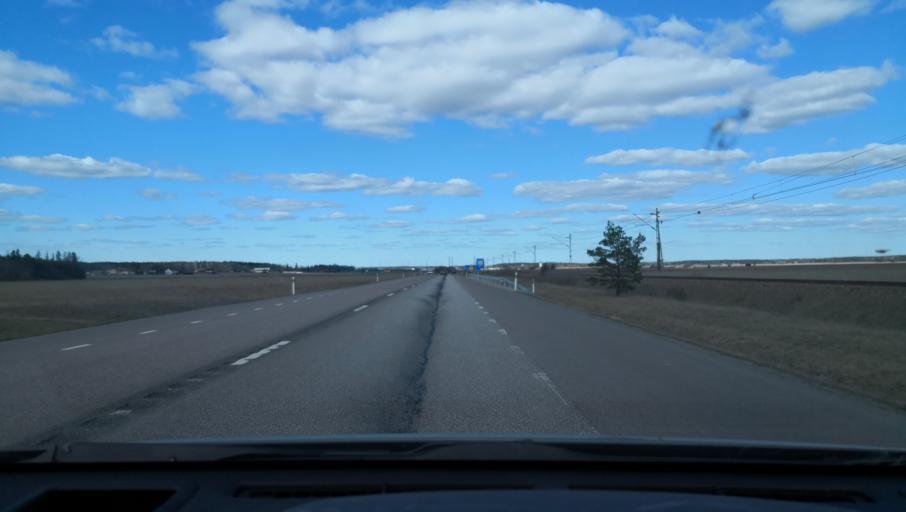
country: SE
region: Vaestmanland
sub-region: Sala Kommun
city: Sala
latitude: 59.8812
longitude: 16.6252
